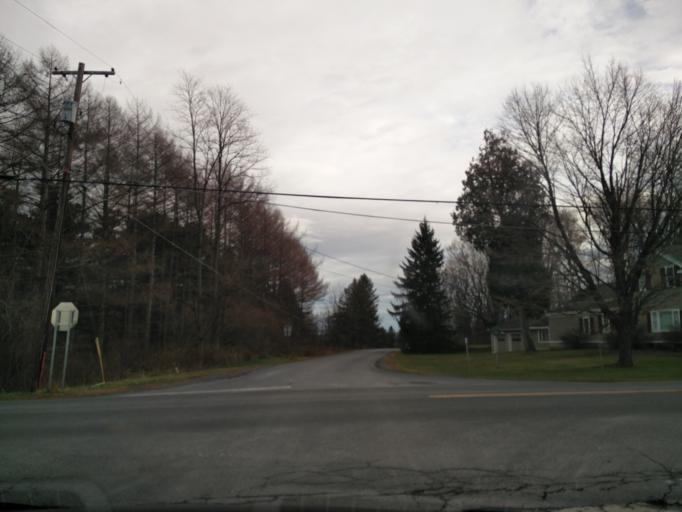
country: US
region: New York
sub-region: Tompkins County
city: Trumansburg
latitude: 42.5266
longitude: -76.6814
